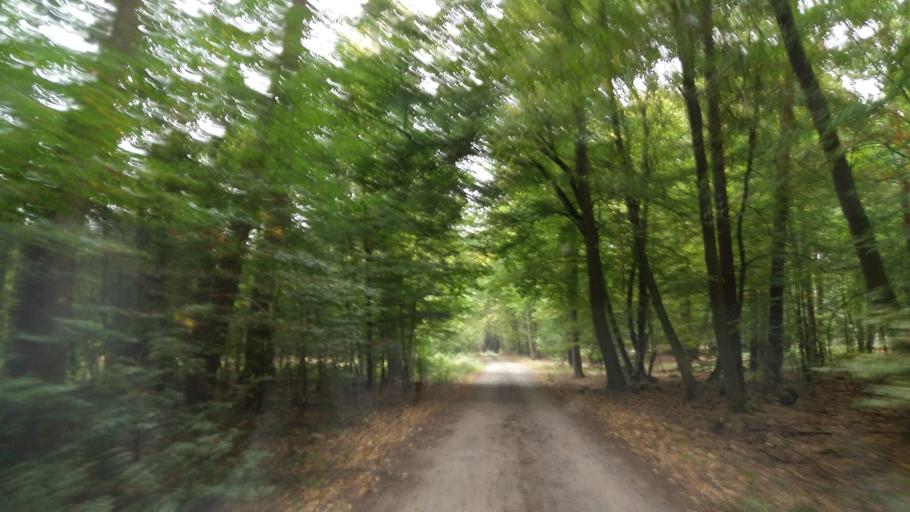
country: PL
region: West Pomeranian Voivodeship
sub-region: Powiat choszczenski
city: Pelczyce
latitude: 52.9620
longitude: 15.3216
